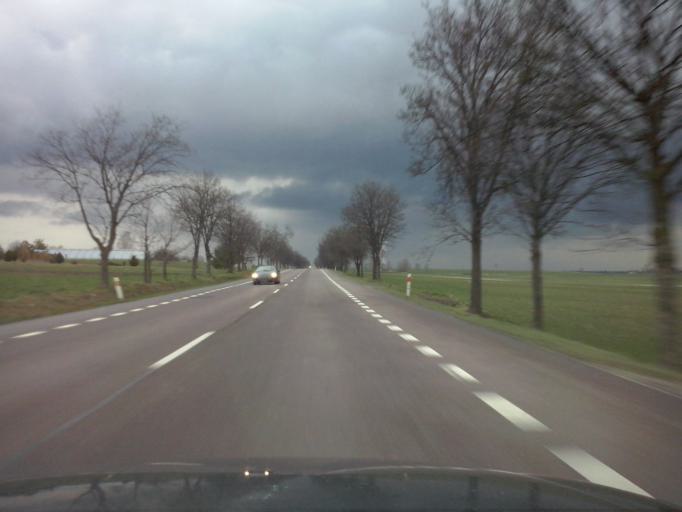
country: PL
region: Lublin Voivodeship
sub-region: Powiat chelmski
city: Rejowiec Fabryczny
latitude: 51.1767
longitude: 23.2337
